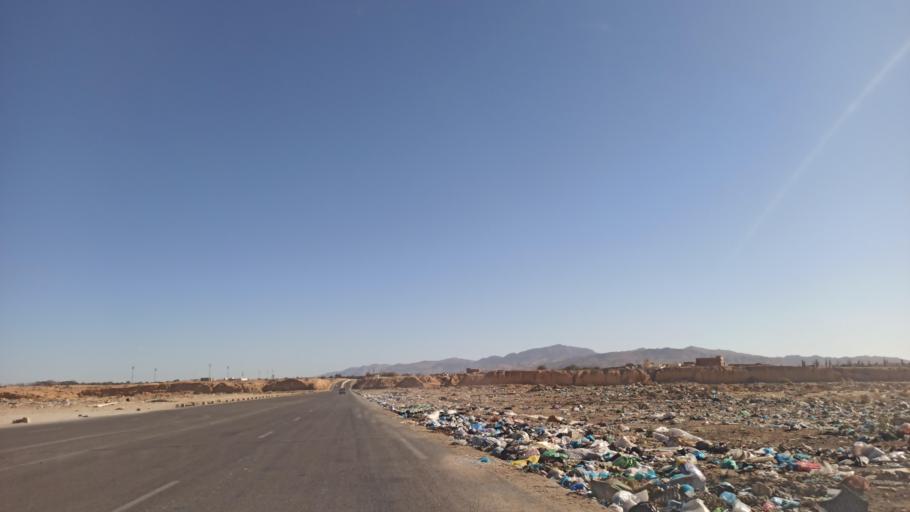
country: TN
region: Gafsa
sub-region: Gafsa Municipality
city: Gafsa
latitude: 34.4340
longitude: 8.8021
